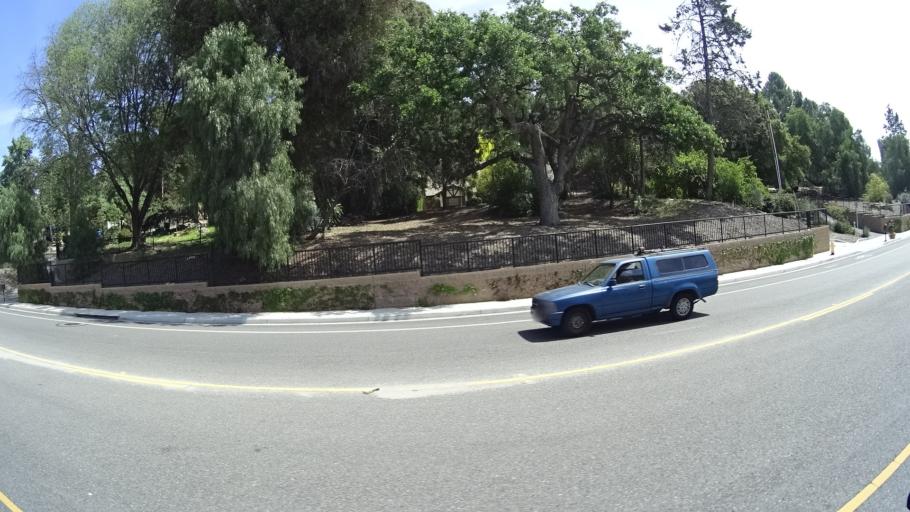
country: US
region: California
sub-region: Ventura County
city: Thousand Oaks
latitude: 34.1838
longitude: -118.8480
